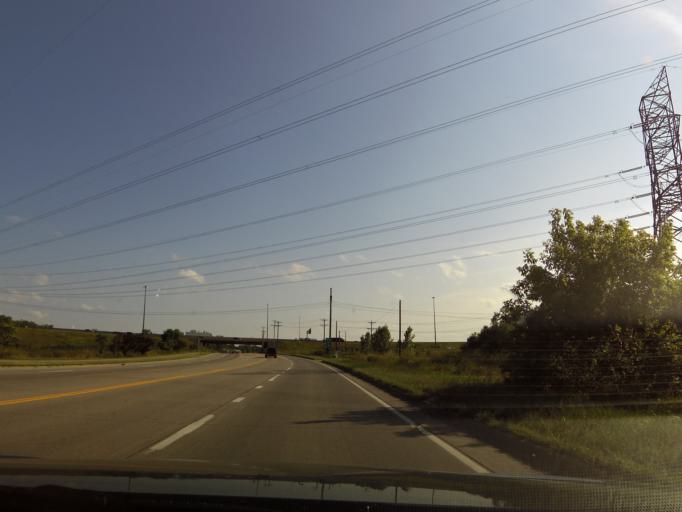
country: US
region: Minnesota
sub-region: Washington County
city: Newport
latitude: 44.8872
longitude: -93.0094
